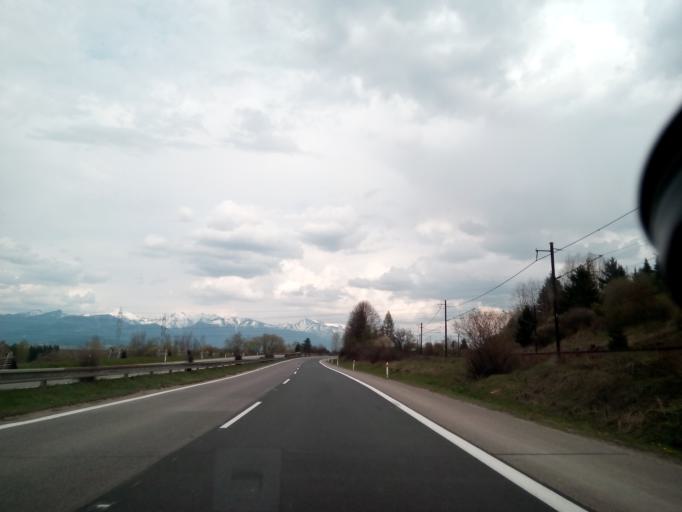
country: SK
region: Zilinsky
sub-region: Okres Liptovsky Mikulas
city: Liptovsky Mikulas
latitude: 49.0892
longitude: 19.4801
